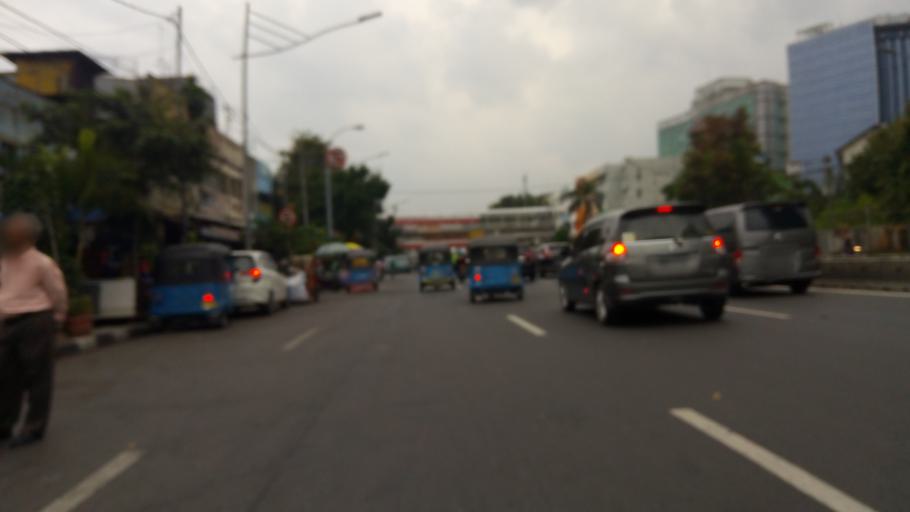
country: ID
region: Jakarta Raya
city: Jakarta
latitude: -6.1731
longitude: 106.8409
